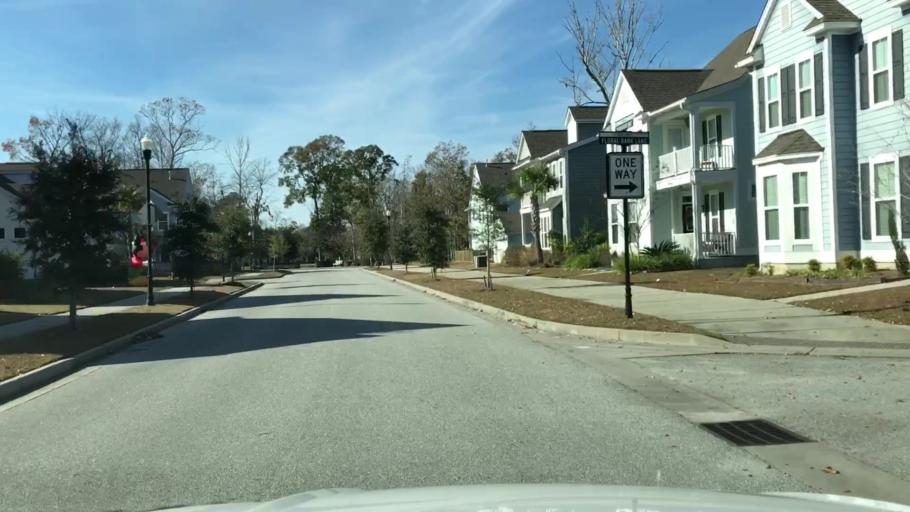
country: US
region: South Carolina
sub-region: Charleston County
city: Shell Point
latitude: 32.8090
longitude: -80.0707
